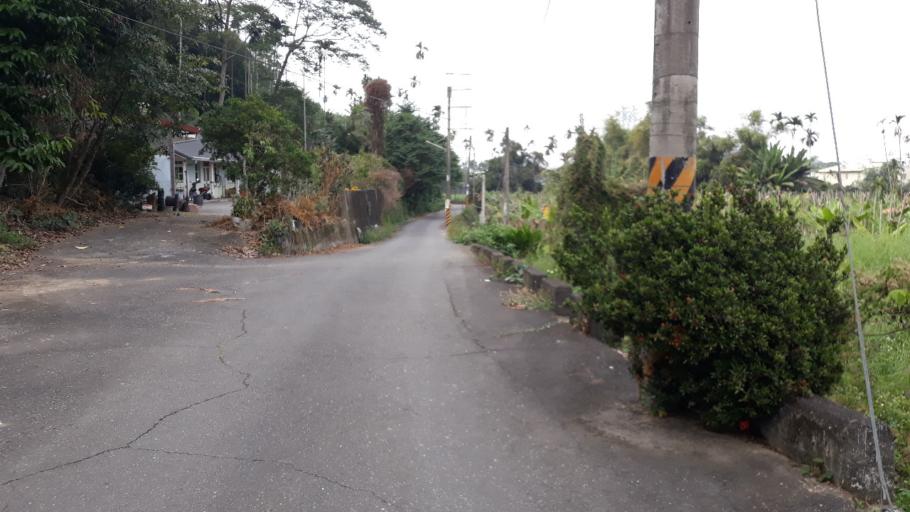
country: TW
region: Taiwan
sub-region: Chiayi
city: Jiayi Shi
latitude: 23.4274
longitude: 120.5254
